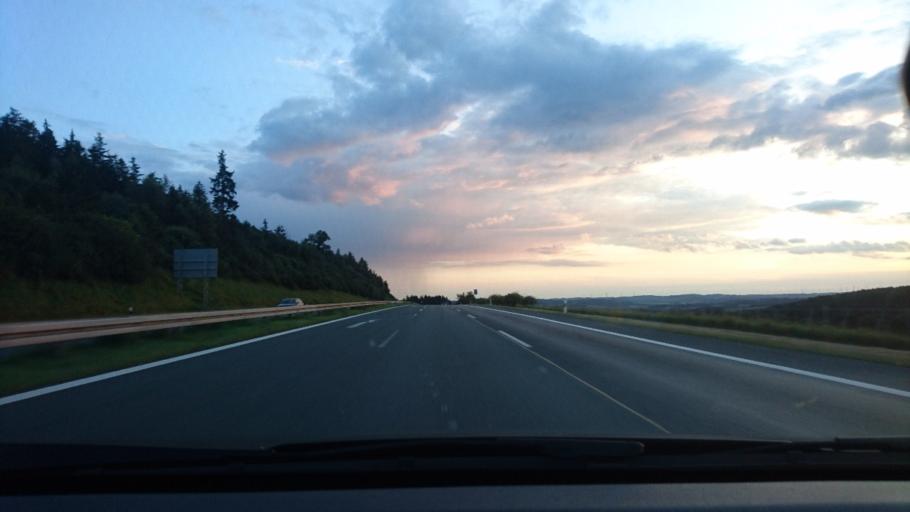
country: DE
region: Saxony
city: Oelsnitz
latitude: 50.4503
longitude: 12.1689
